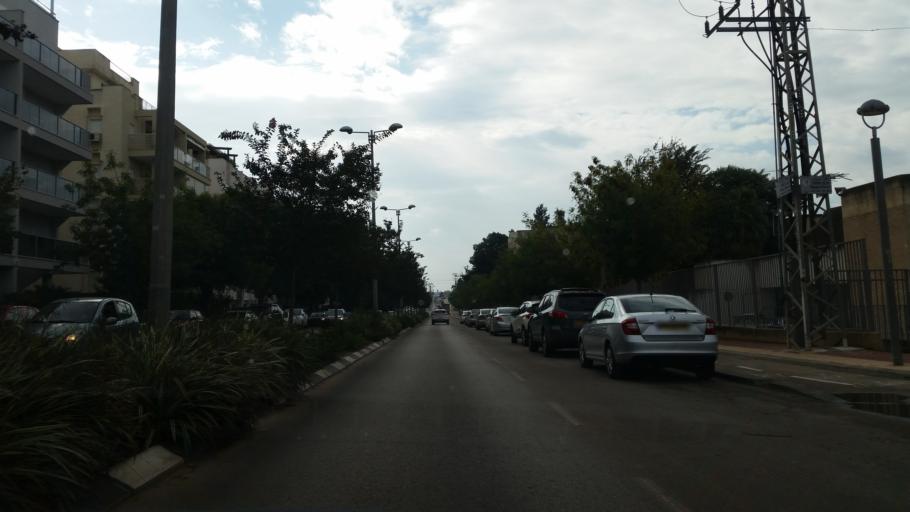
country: IL
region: Central District
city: Ra'anana
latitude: 32.1774
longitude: 34.8699
